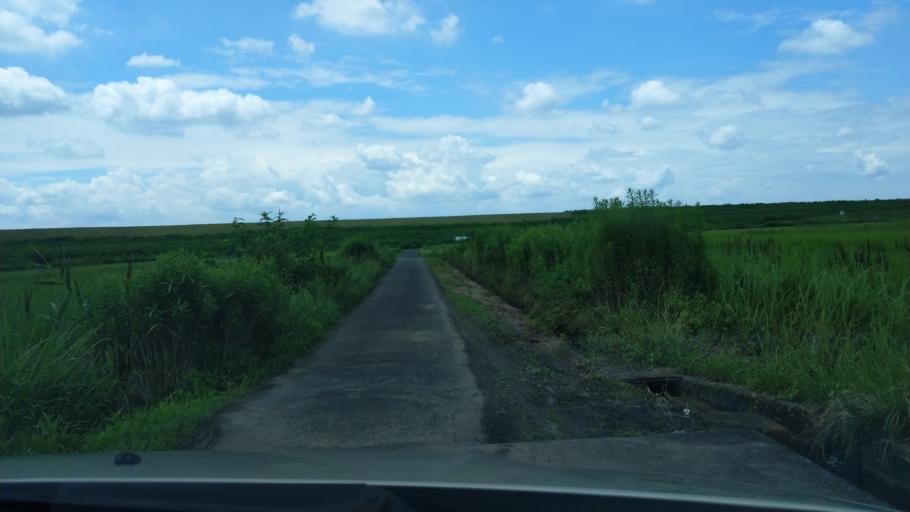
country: JP
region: Saitama
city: Shiki
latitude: 35.8812
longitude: 139.5853
